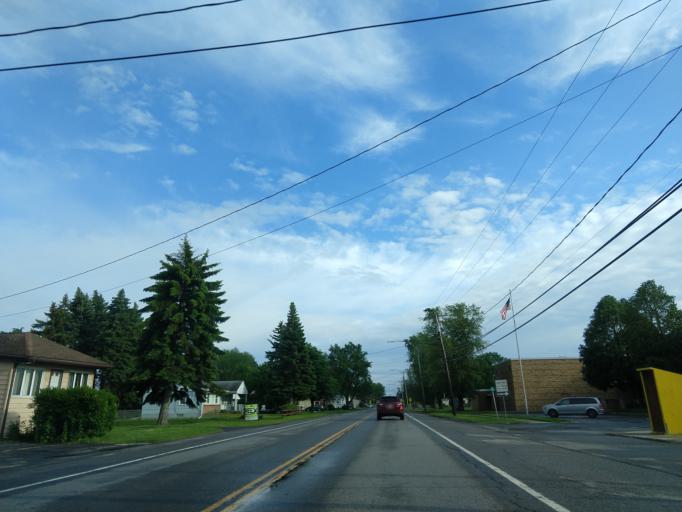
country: US
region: New York
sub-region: Erie County
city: West Seneca
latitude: 42.8616
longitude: -78.7875
